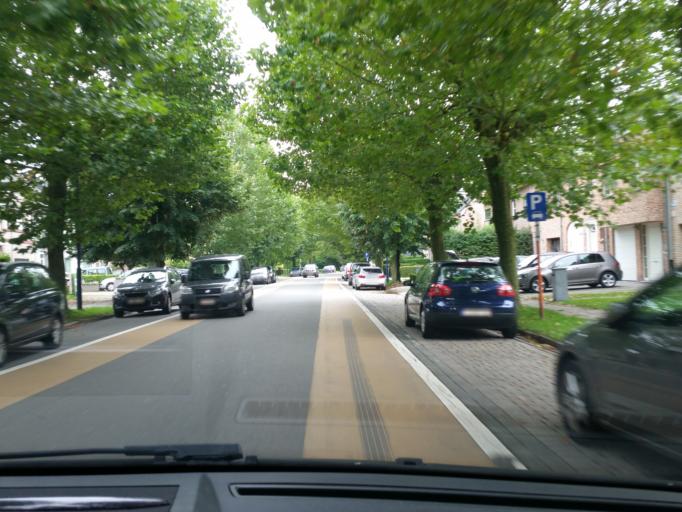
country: BE
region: Flanders
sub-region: Provincie Antwerpen
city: Kontich
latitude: 51.1269
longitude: 4.4485
